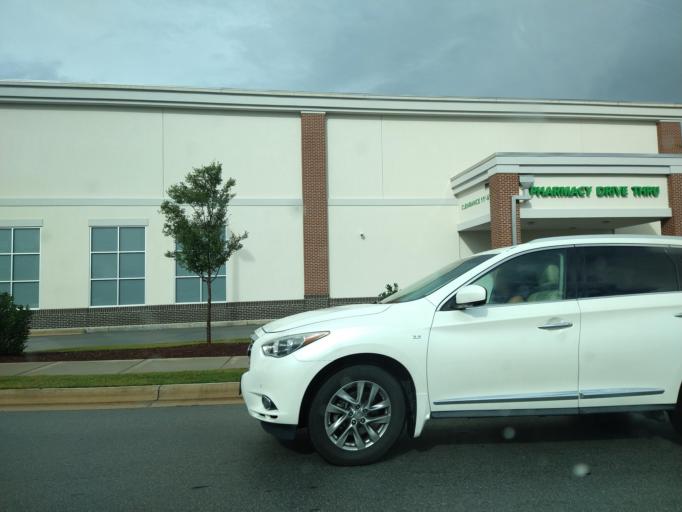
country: US
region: North Carolina
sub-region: Onslow County
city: Pumpkin Center
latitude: 34.7960
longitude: -77.4089
